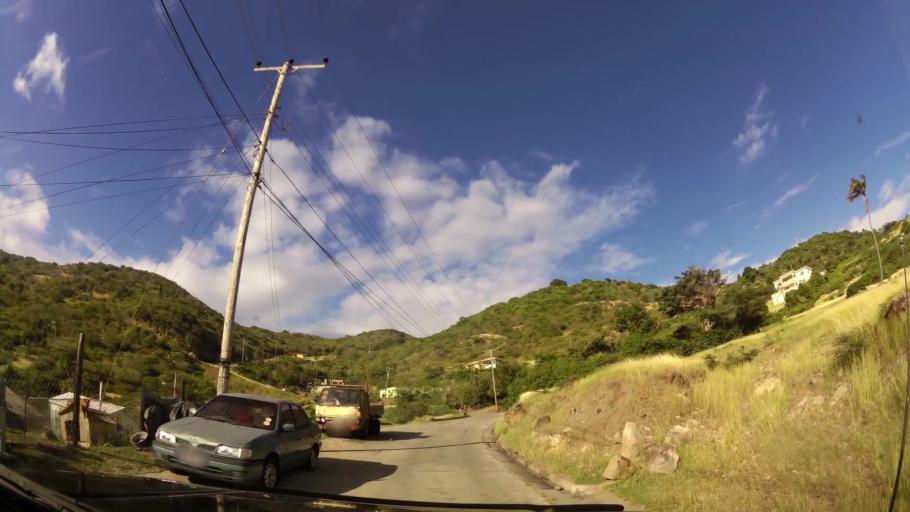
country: MS
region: Saint Peter
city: Brades
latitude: 16.8005
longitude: -62.1944
